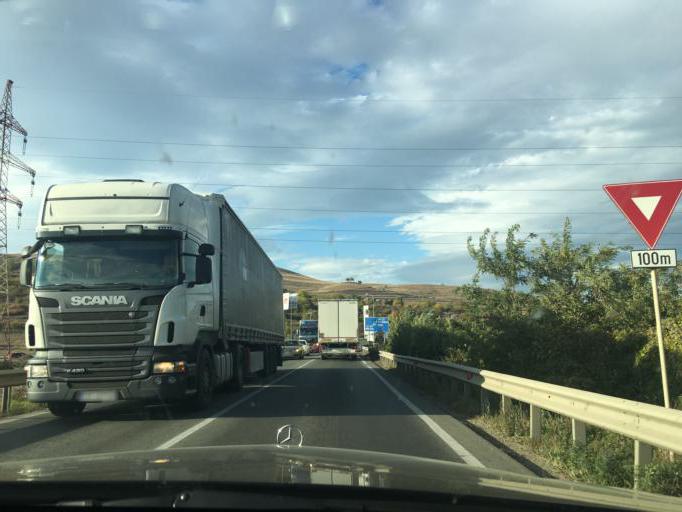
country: RO
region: Alba
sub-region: Municipiul Alba Iulia
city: Barabant
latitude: 46.1058
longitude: 23.6088
